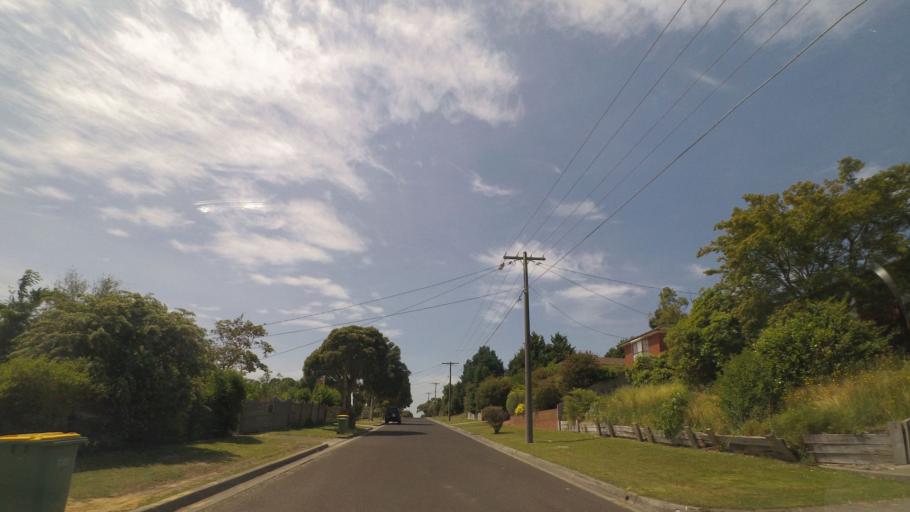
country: AU
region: Victoria
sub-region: Yarra Ranges
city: Chirnside Park
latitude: -37.7567
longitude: 145.3152
